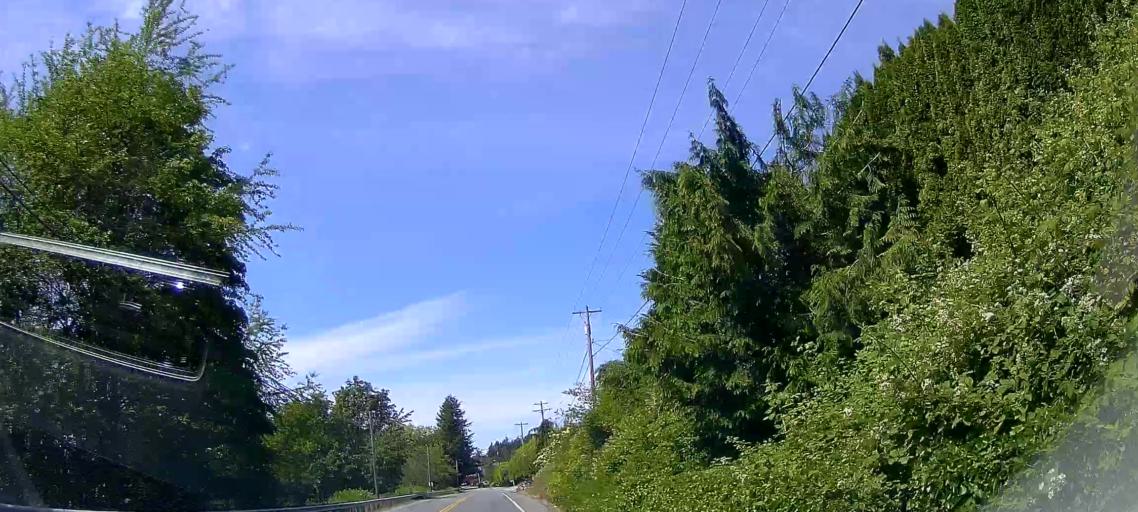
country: US
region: Washington
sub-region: Snohomish County
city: Stanwood
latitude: 48.2476
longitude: -122.3497
